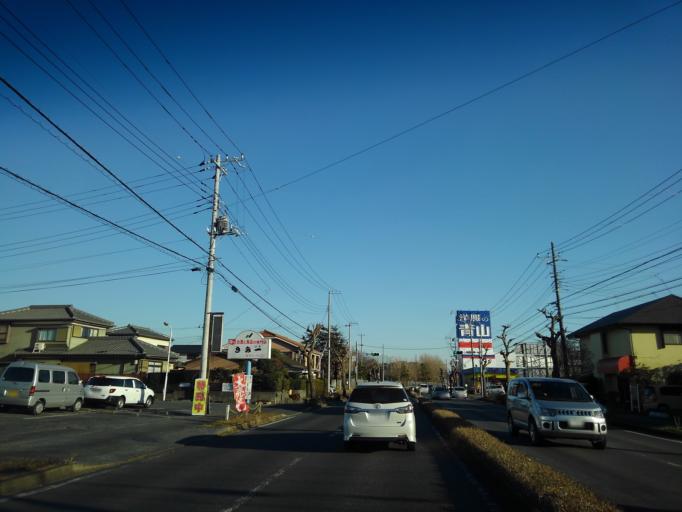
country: JP
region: Chiba
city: Kimitsu
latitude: 35.3262
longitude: 139.9076
